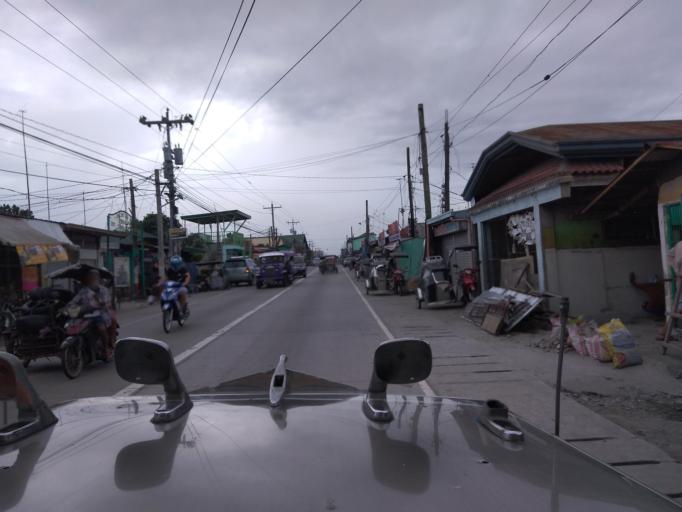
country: PH
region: Central Luzon
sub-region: Province of Pampanga
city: Pandacaqui
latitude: 15.1825
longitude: 120.6289
